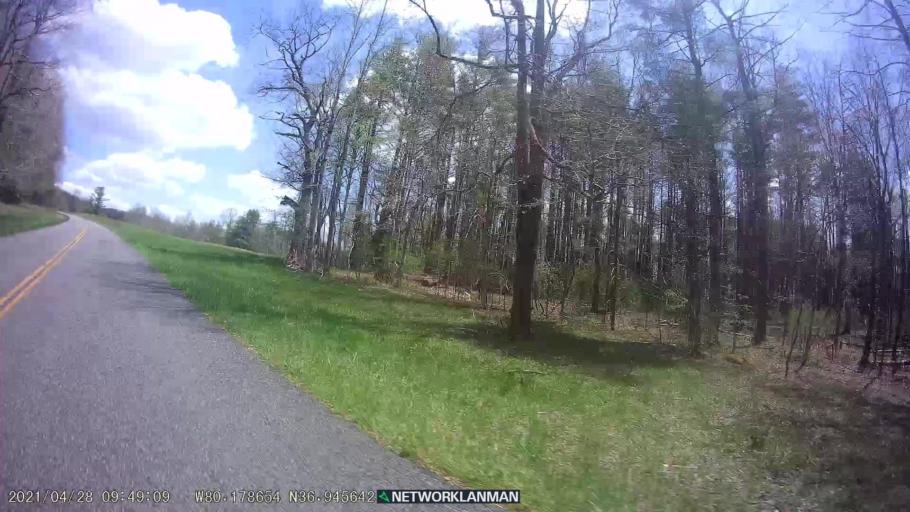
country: US
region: Virginia
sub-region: Floyd County
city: Floyd
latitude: 36.9457
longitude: -80.1786
